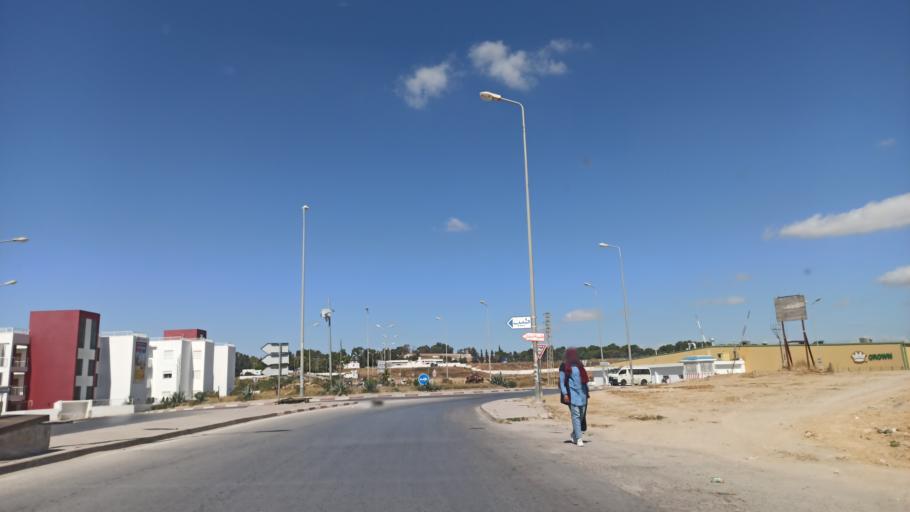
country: TN
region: Manouba
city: Manouba
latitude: 36.7834
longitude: 10.0757
